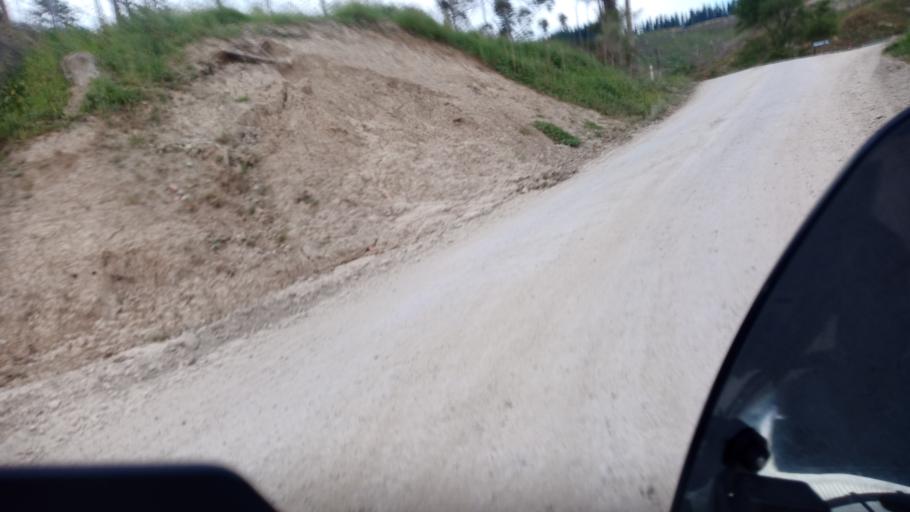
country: NZ
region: Gisborne
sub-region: Gisborne District
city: Gisborne
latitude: -38.4682
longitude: 177.9754
